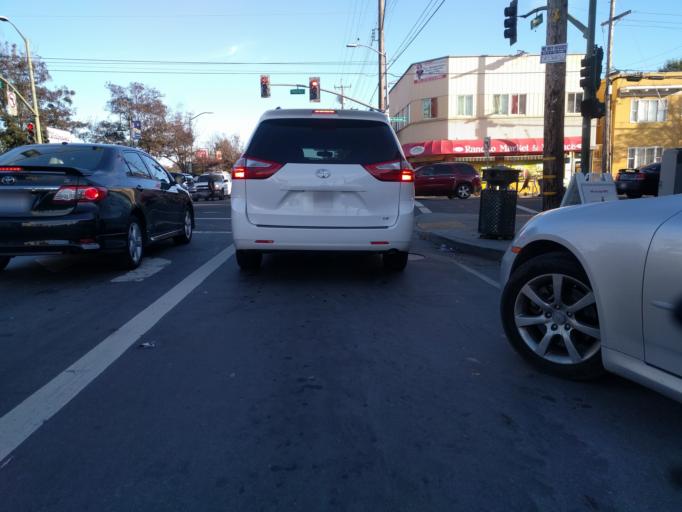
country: US
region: California
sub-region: Alameda County
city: Alameda
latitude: 37.7838
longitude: -122.2231
